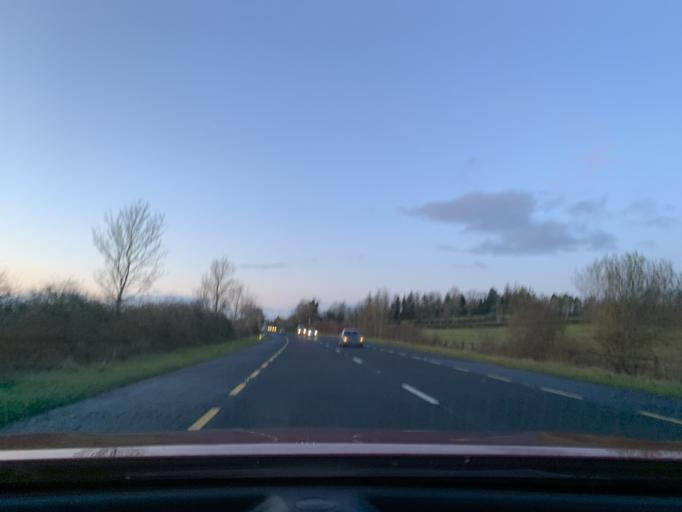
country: IE
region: Connaught
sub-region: County Leitrim
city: Carrick-on-Shannon
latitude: 53.9063
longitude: -7.9612
